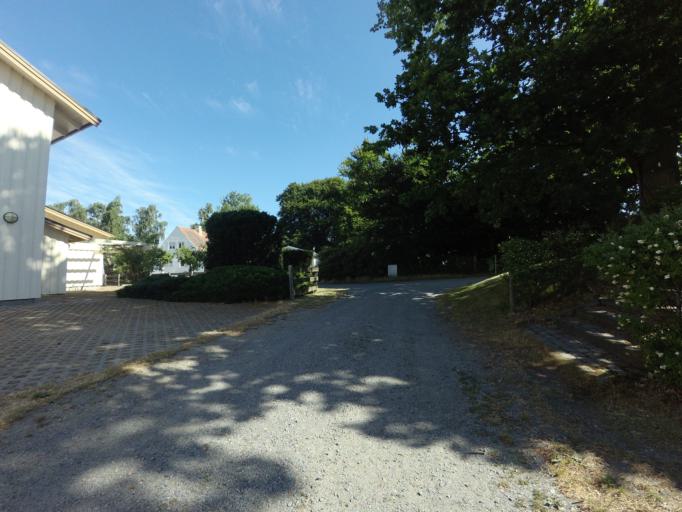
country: SE
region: Skane
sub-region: Vellinge Kommun
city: Skanor med Falsterbo
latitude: 55.3870
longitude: 12.8254
